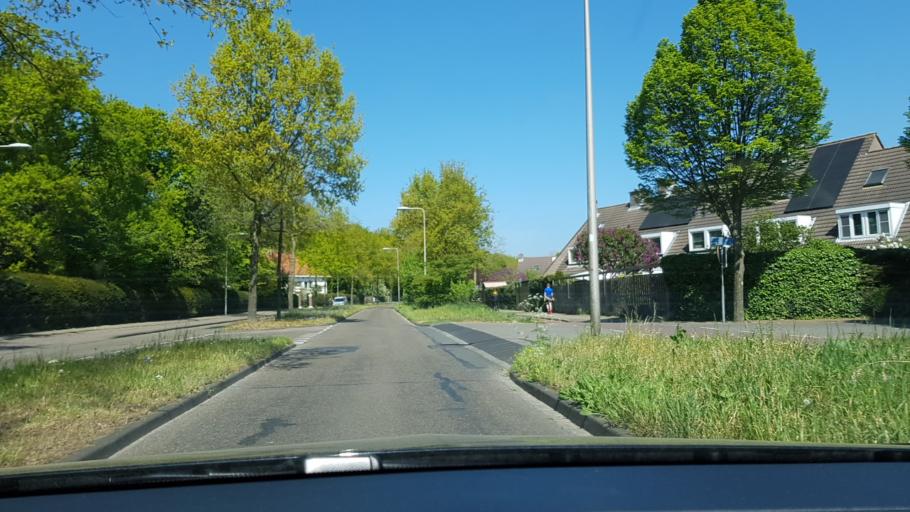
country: NL
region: North Holland
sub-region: Gemeente Heemstede
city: Heemstede
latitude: 52.3345
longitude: 4.6160
